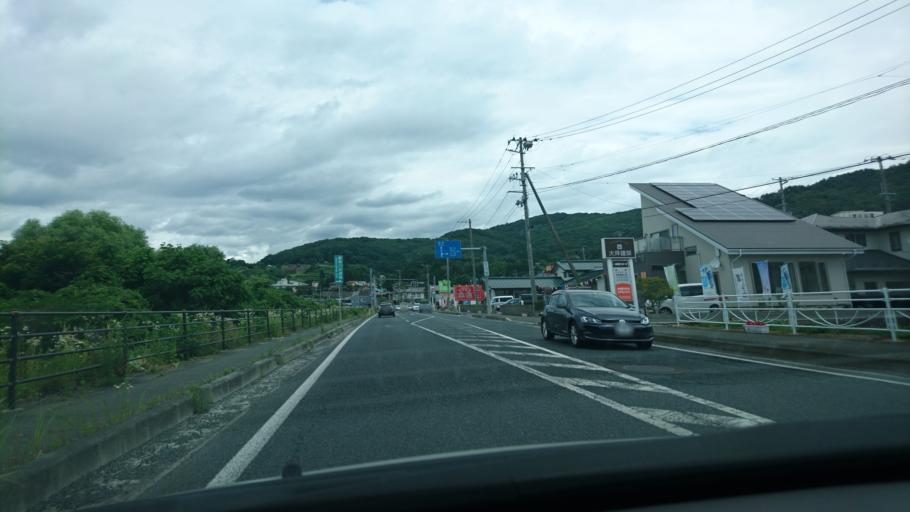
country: JP
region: Iwate
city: Morioka-shi
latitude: 39.6552
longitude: 141.1822
